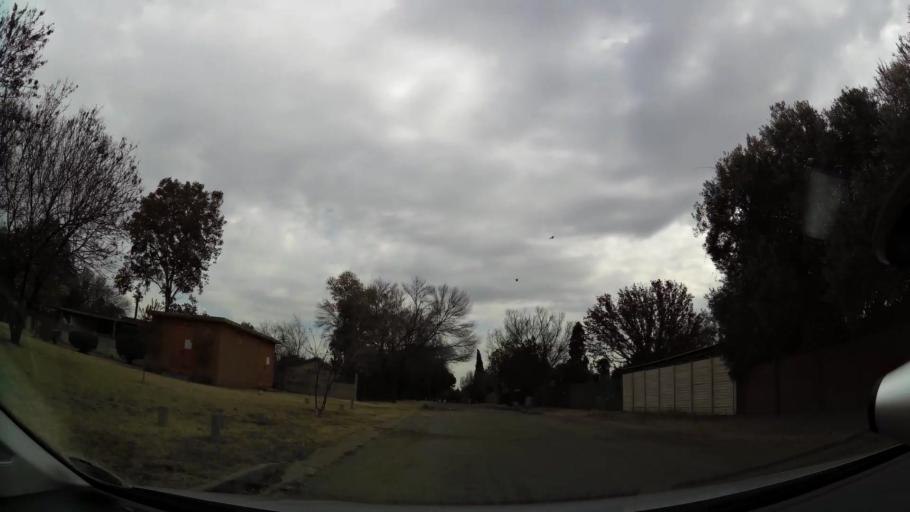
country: ZA
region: Orange Free State
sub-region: Fezile Dabi District Municipality
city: Kroonstad
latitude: -27.6793
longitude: 27.2391
